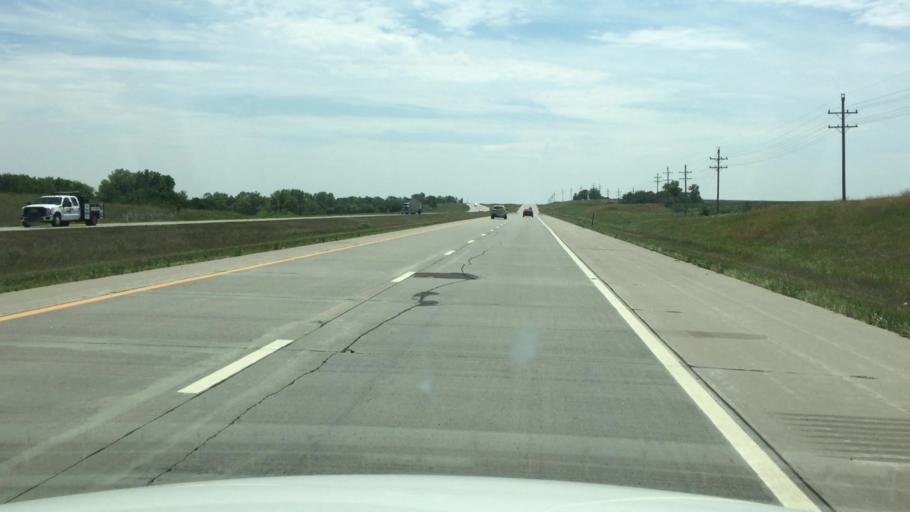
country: US
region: Kansas
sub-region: Shawnee County
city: Topeka
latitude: 39.2293
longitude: -95.7196
